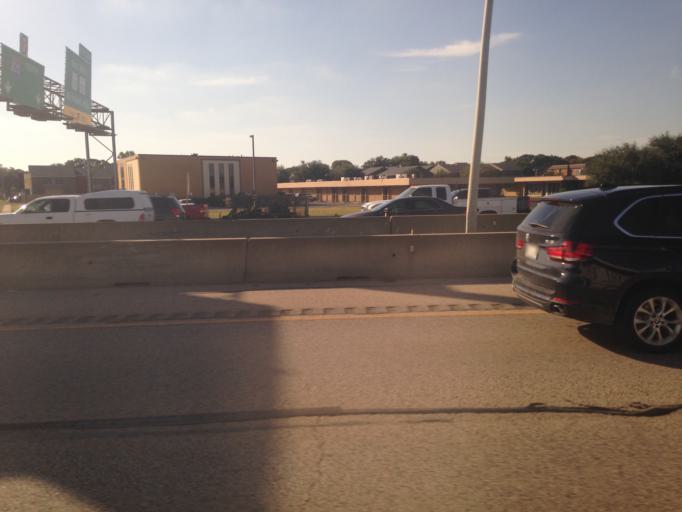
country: US
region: Texas
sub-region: Tarrant County
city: Richland Hills
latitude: 32.8115
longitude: -97.2087
